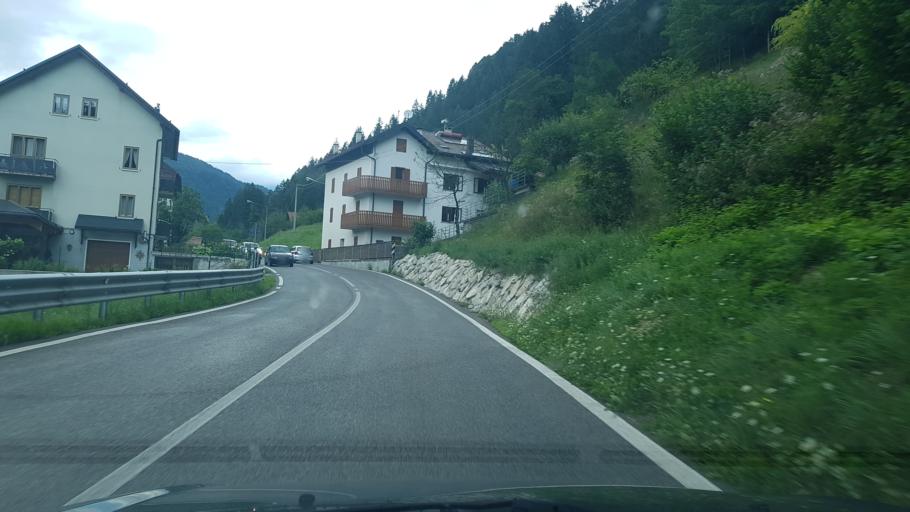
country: IT
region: Friuli Venezia Giulia
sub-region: Provincia di Udine
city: Ovaro
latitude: 46.4964
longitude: 12.8668
